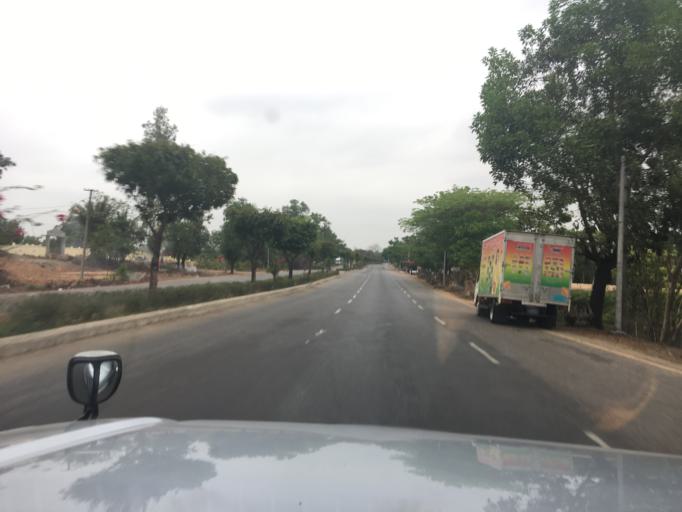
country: MM
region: Bago
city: Thanatpin
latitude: 17.2032
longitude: 96.4117
